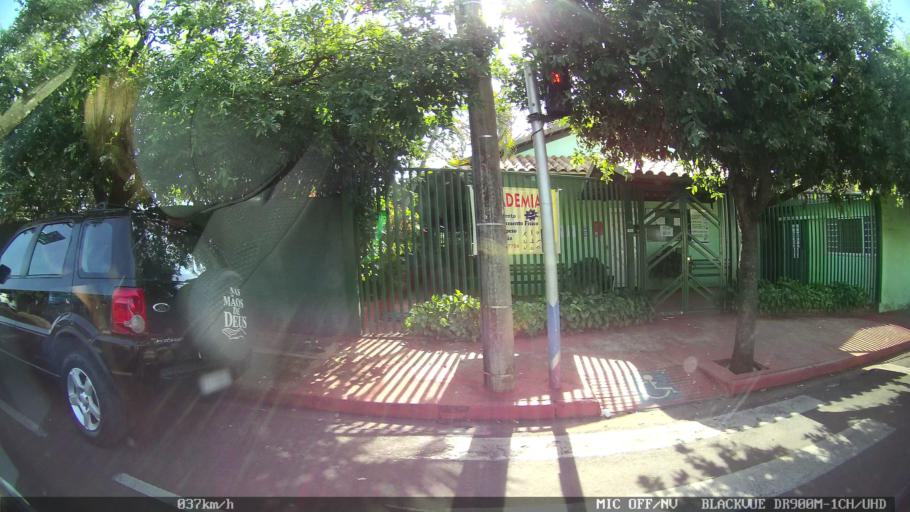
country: BR
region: Sao Paulo
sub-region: Sao Jose Do Rio Preto
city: Sao Jose do Rio Preto
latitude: -20.7929
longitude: -49.3815
